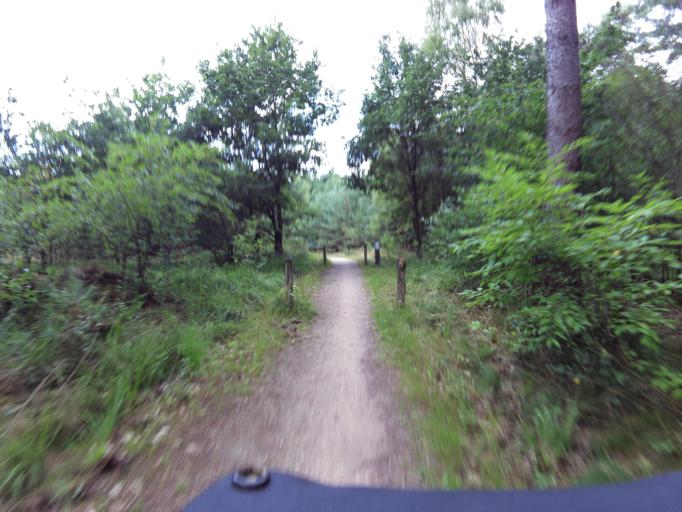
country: NL
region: Limburg
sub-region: Gemeente Roerdalen
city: Vlodrop
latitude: 51.1524
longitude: 6.1087
